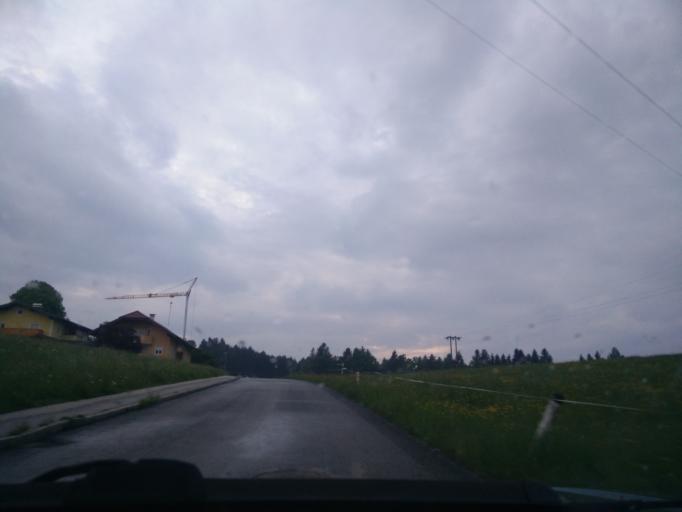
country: AT
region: Salzburg
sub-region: Politischer Bezirk Salzburg-Umgebung
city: Seekirchen am Wallersee
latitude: 47.8978
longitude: 13.1117
